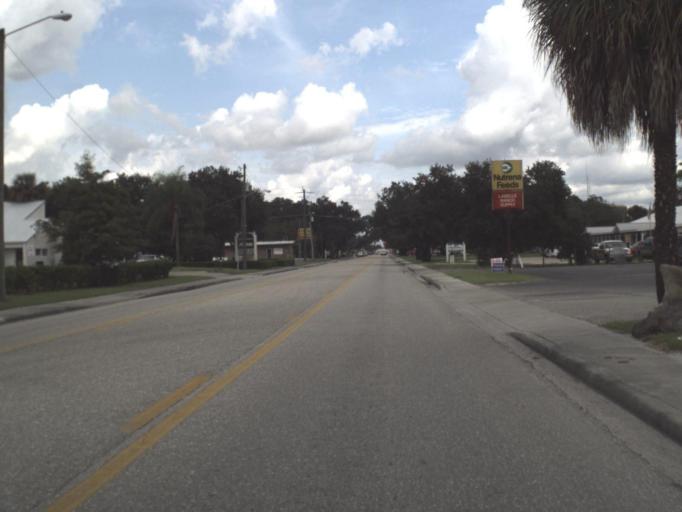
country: US
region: Florida
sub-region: Hendry County
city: LaBelle
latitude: 26.7574
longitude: -81.4373
